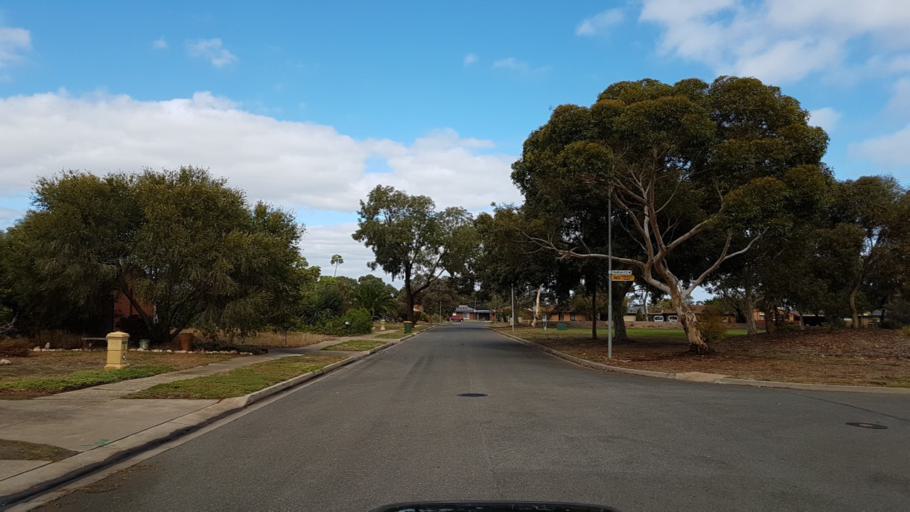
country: AU
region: South Australia
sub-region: Charles Sturt
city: Seaton
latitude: -34.9082
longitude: 138.5196
